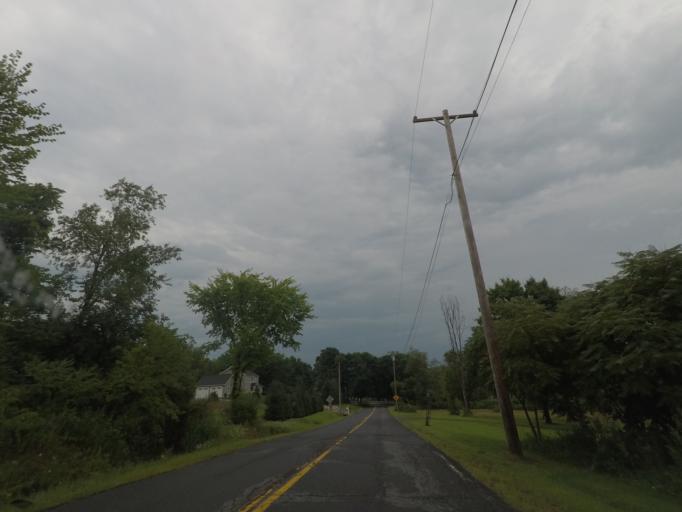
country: US
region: New York
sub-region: Rensselaer County
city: Poestenkill
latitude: 42.8038
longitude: -73.5591
